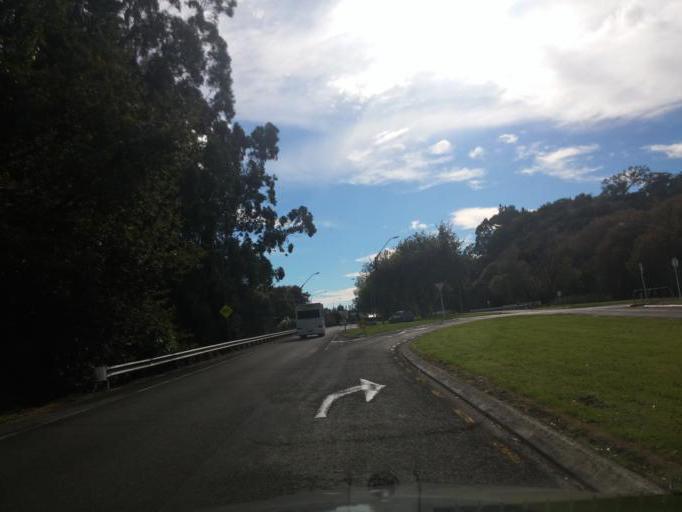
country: NZ
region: Manawatu-Wanganui
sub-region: Palmerston North City
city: Palmerston North
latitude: -40.3819
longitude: 175.6151
